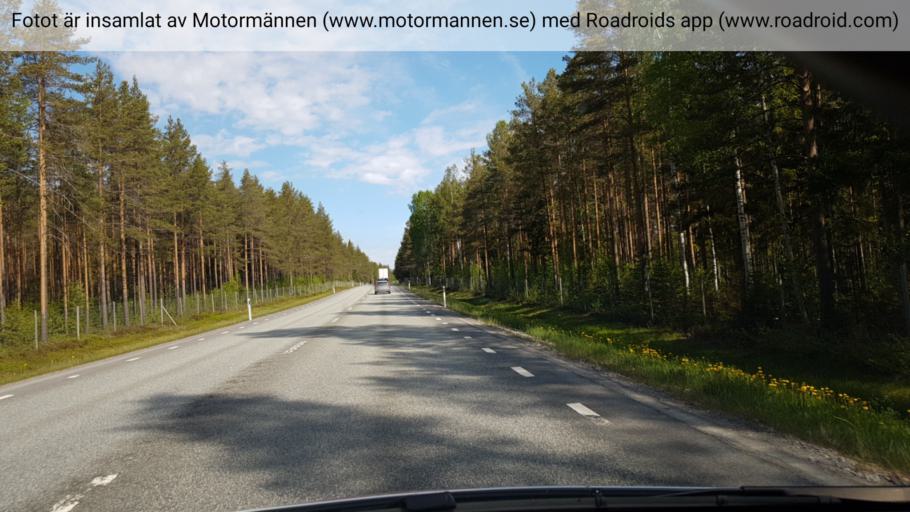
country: SE
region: Vaesterbotten
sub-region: Skelleftea Kommun
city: Burea
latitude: 64.5238
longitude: 21.2588
